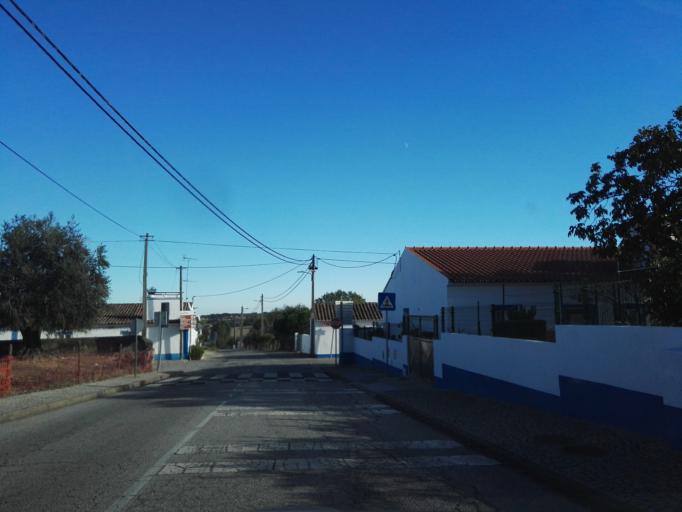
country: PT
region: Evora
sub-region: Arraiolos
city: Arraiolos
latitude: 38.6544
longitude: -7.9823
